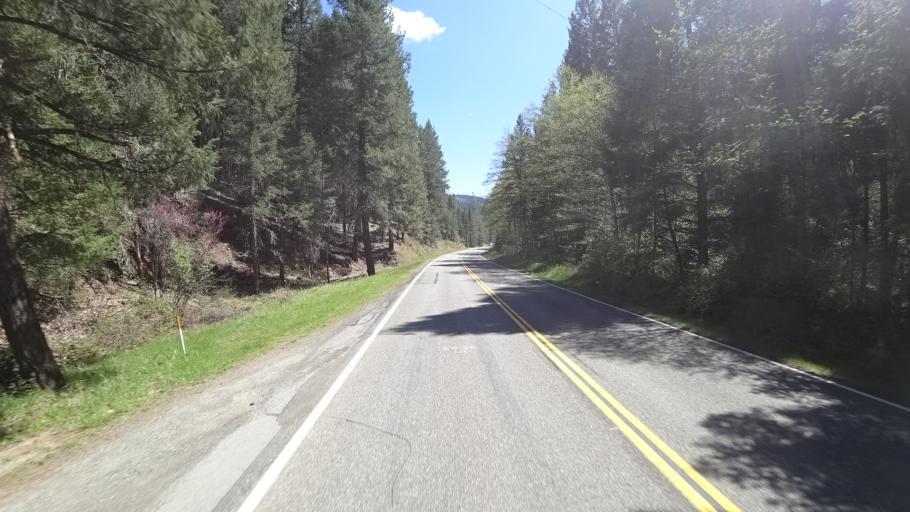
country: US
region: California
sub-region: Trinity County
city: Weaverville
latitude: 40.7635
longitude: -122.8879
